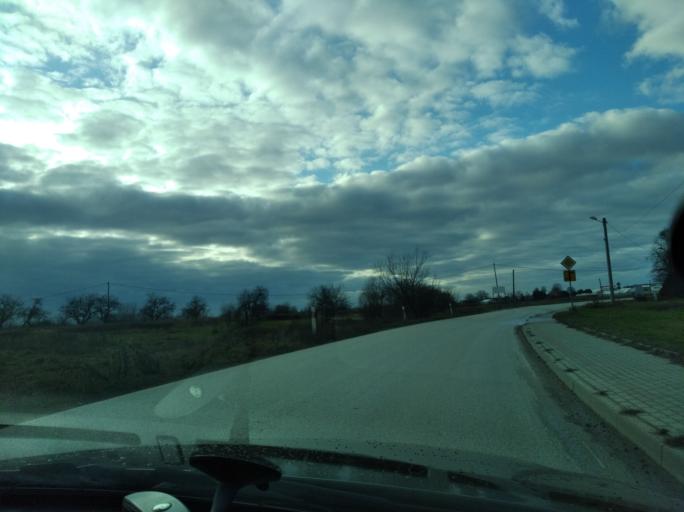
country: PL
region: Subcarpathian Voivodeship
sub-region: Powiat lancucki
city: Czarna
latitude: 50.1130
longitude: 22.2160
